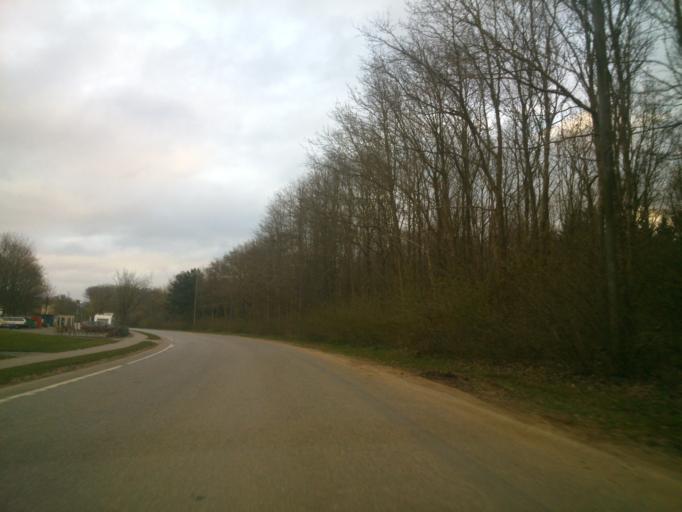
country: DK
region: South Denmark
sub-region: Fredericia Kommune
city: Snoghoj
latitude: 55.5582
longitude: 9.7126
